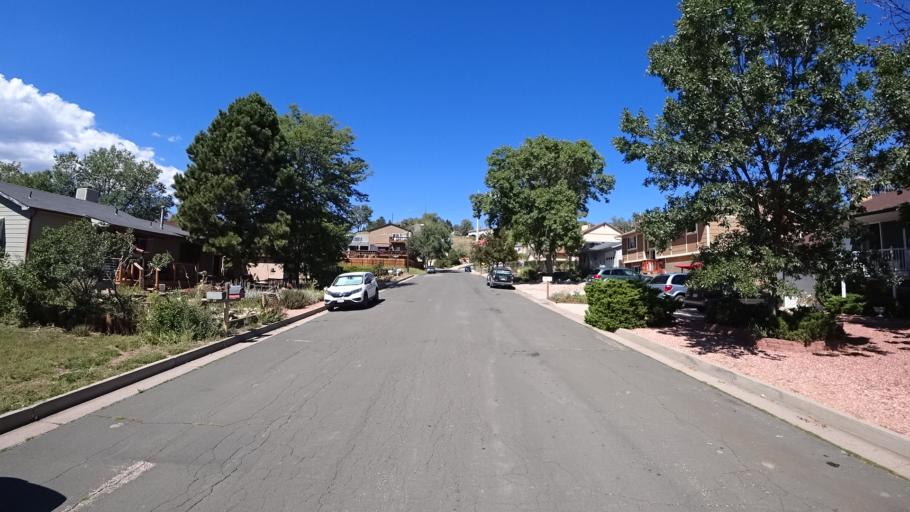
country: US
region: Colorado
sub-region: El Paso County
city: Colorado Springs
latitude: 38.8540
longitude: -104.8574
